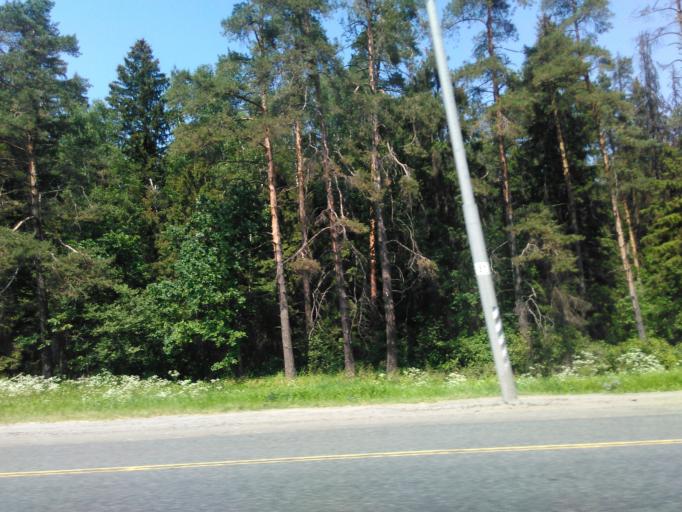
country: RU
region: Moskovskaya
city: Zarya
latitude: 55.8096
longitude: 38.0762
